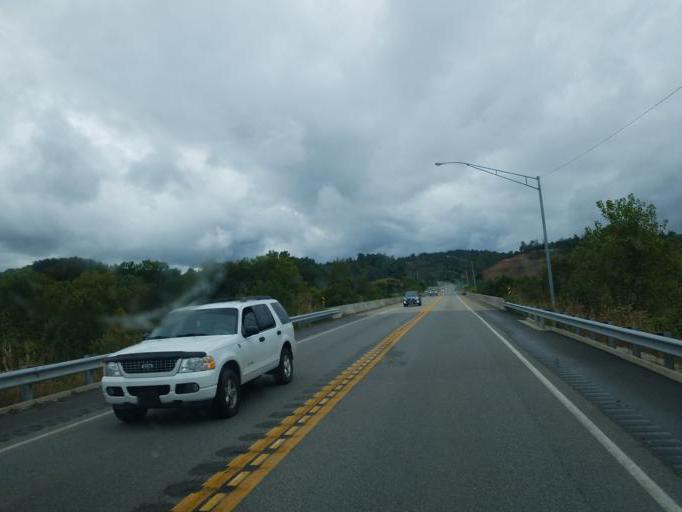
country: US
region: Ohio
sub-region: Scioto County
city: Franklin Furnace
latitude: 38.6465
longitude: -82.8692
